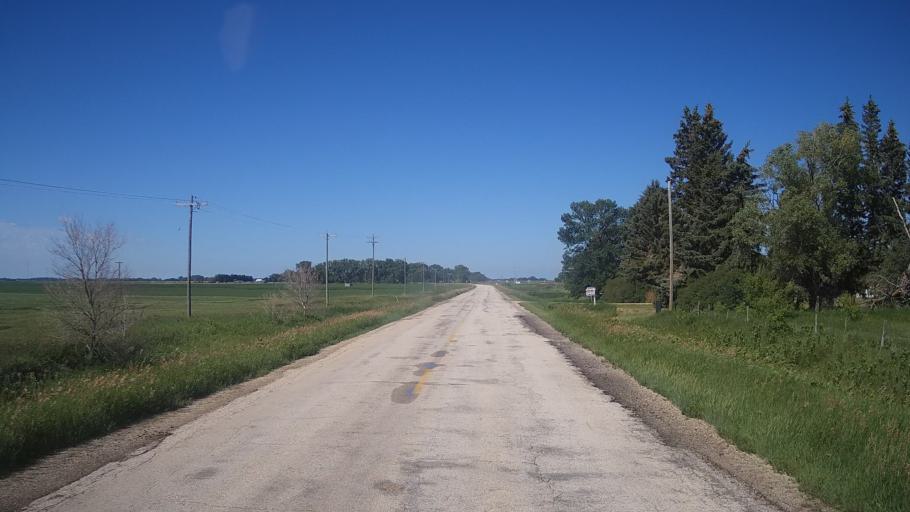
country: CA
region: Manitoba
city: Portage la Prairie
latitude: 50.0429
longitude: -98.0606
